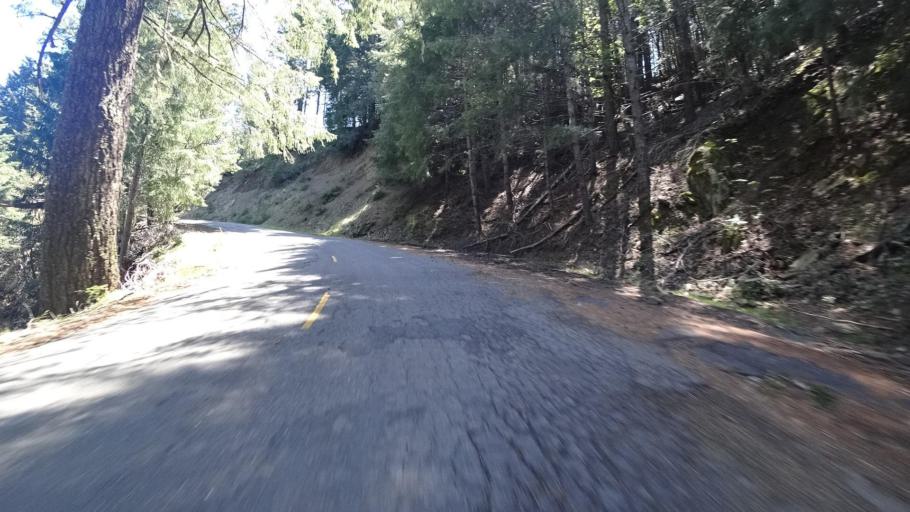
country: US
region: California
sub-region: Humboldt County
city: Rio Dell
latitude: 40.2925
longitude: -124.0572
